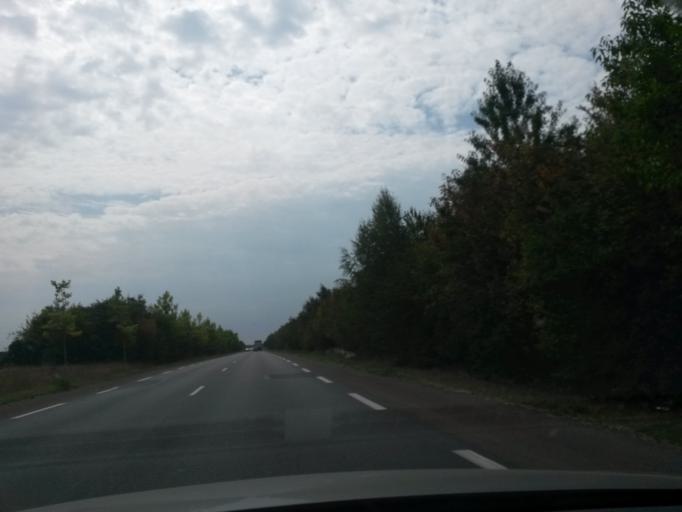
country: FR
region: Poitou-Charentes
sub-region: Departement de la Charente-Maritime
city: Saint-Xandre
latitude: 46.1921
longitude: -1.0946
